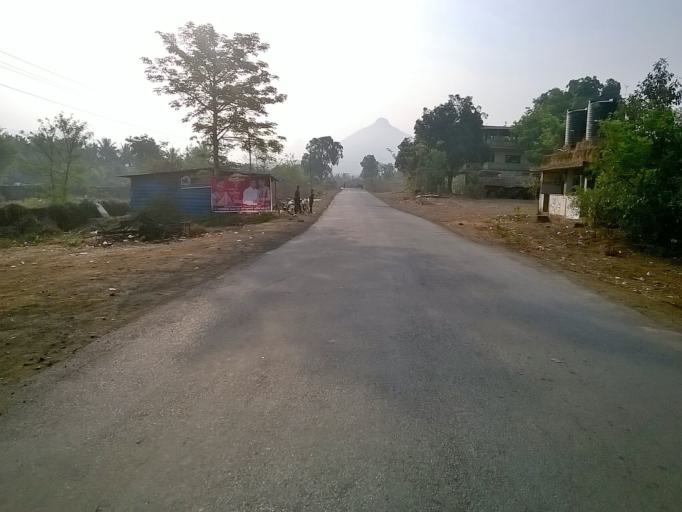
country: IN
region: Maharashtra
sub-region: Raigarh
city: Kalundri
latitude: 19.0180
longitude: 73.1912
